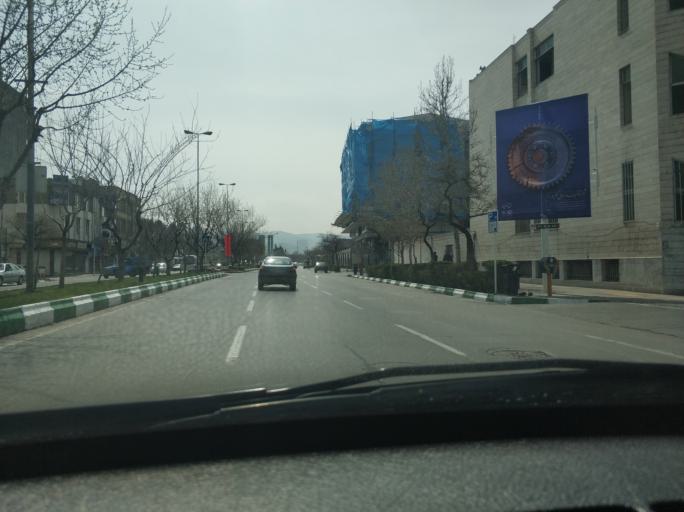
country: IR
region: Razavi Khorasan
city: Mashhad
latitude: 36.3023
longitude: 59.5643
